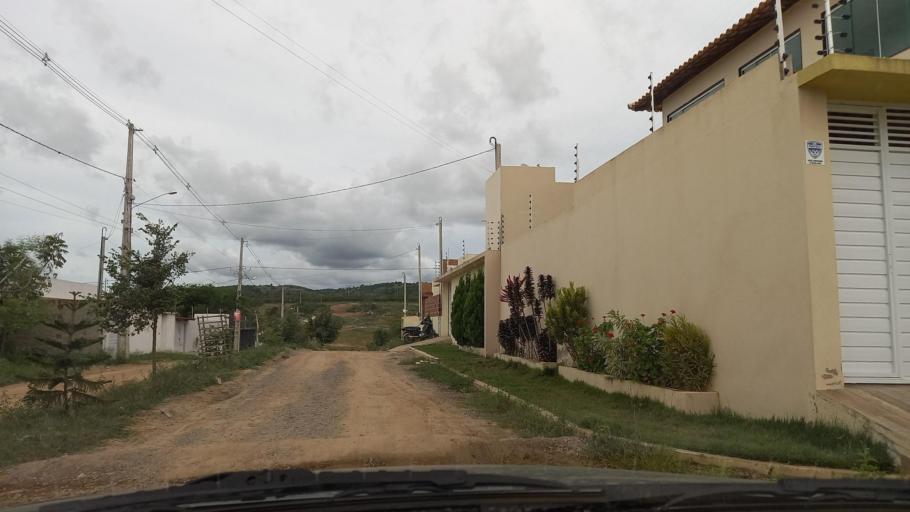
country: BR
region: Pernambuco
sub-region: Gravata
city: Gravata
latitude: -8.2234
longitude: -35.5743
